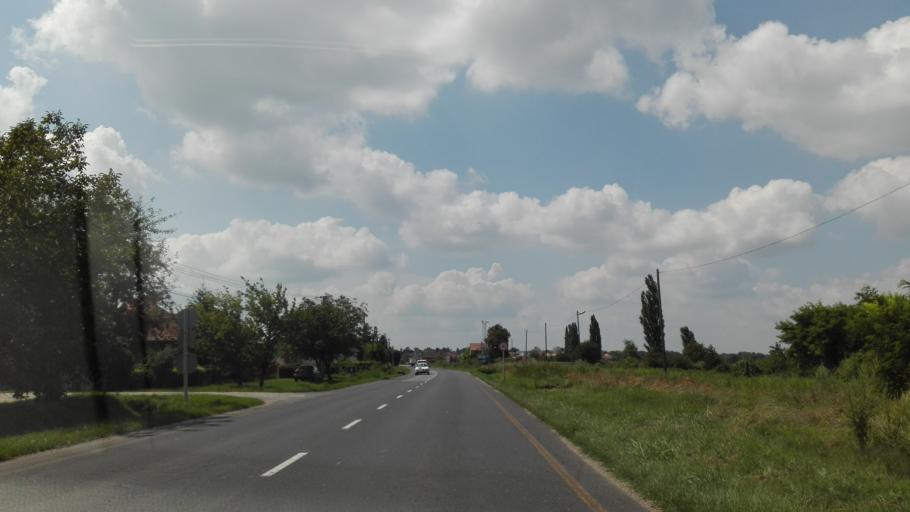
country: HU
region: Fejer
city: Eloszallas
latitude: 46.8316
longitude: 18.8374
